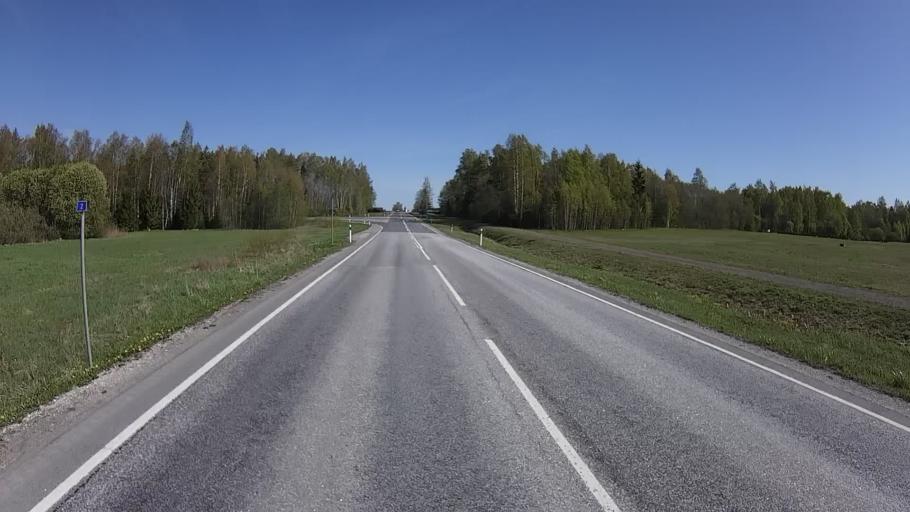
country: EE
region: Raplamaa
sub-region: Rapla vald
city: Rapla
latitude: 58.9885
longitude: 24.7846
